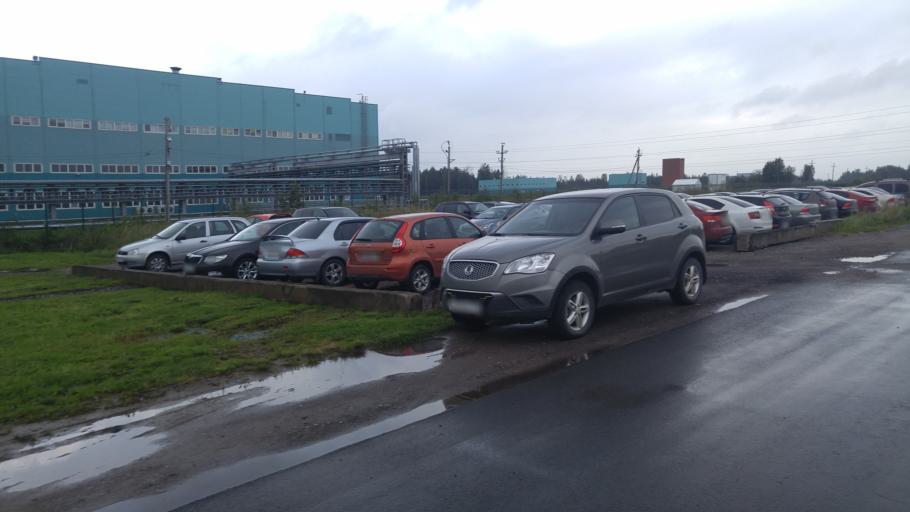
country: RU
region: St.-Petersburg
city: Metallostroy
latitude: 59.7799
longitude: 30.5670
